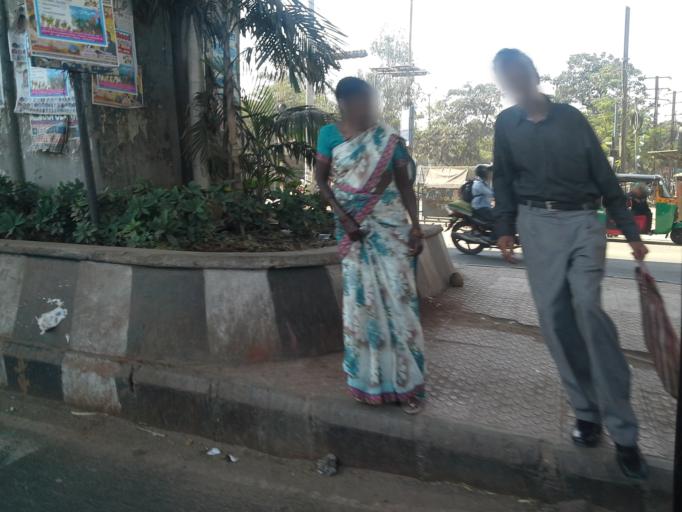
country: IN
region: Telangana
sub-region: Hyderabad
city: Hyderabad
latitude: 17.3770
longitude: 78.4294
